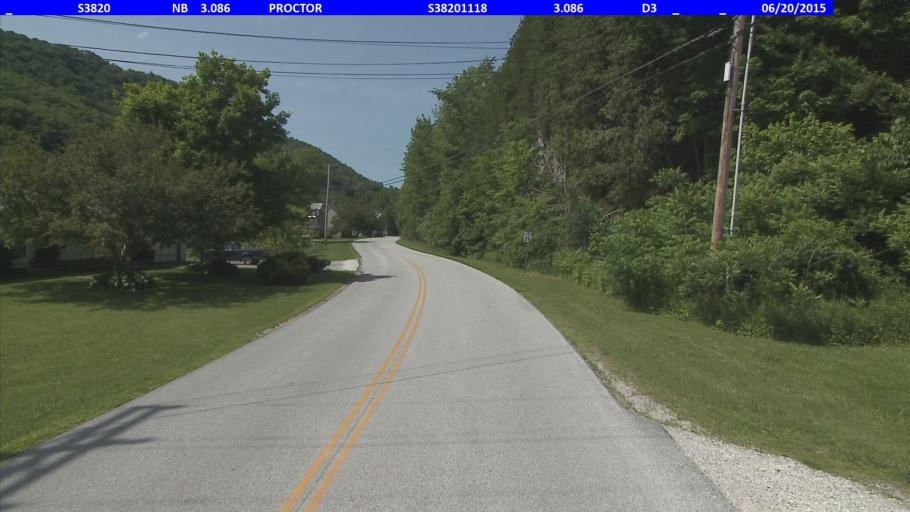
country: US
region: Vermont
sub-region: Rutland County
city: West Rutland
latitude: 43.6532
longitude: -73.0431
